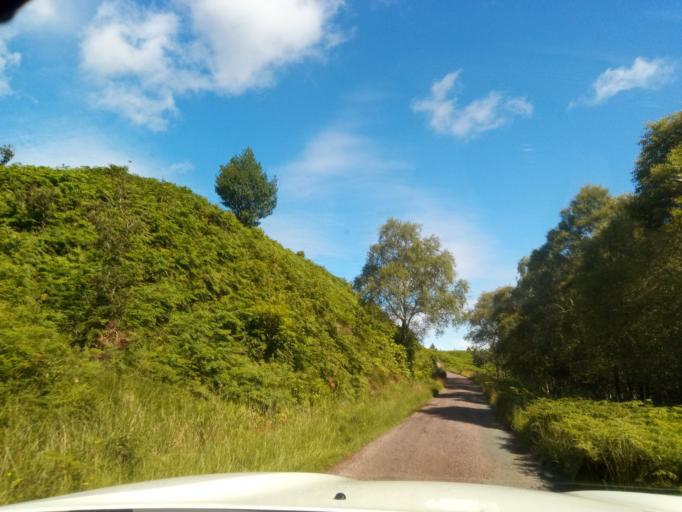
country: GB
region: Scotland
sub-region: Argyll and Bute
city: Isle Of Mull
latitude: 56.7714
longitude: -5.8242
